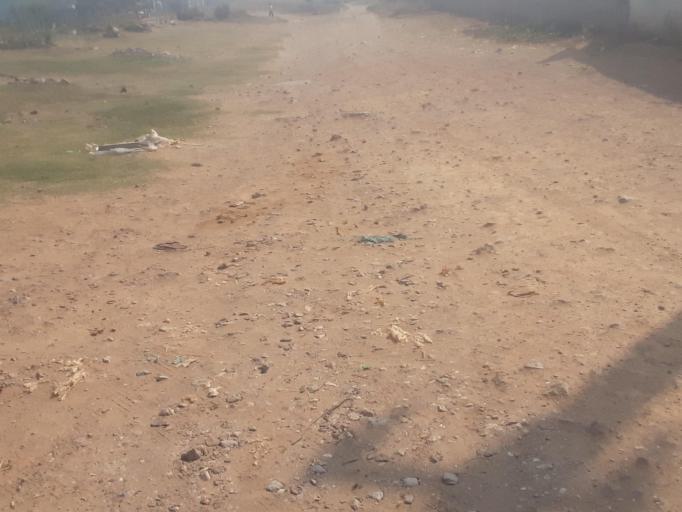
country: ZM
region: Lusaka
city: Lusaka
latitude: -15.3716
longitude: 28.2943
